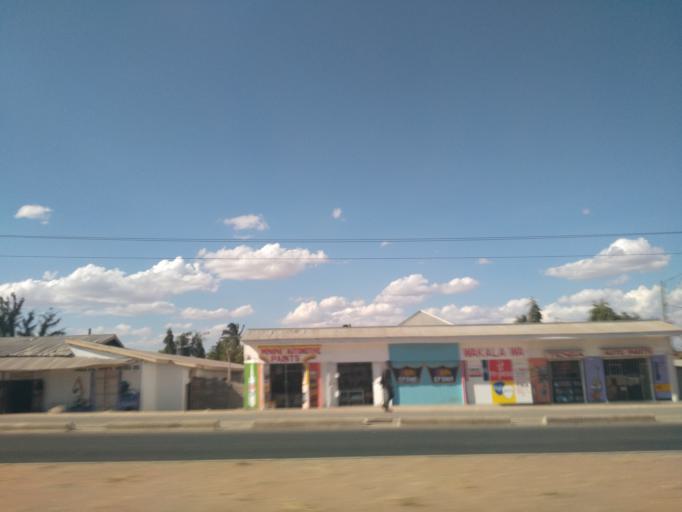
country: TZ
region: Dodoma
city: Dodoma
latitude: -6.1731
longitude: 35.7343
